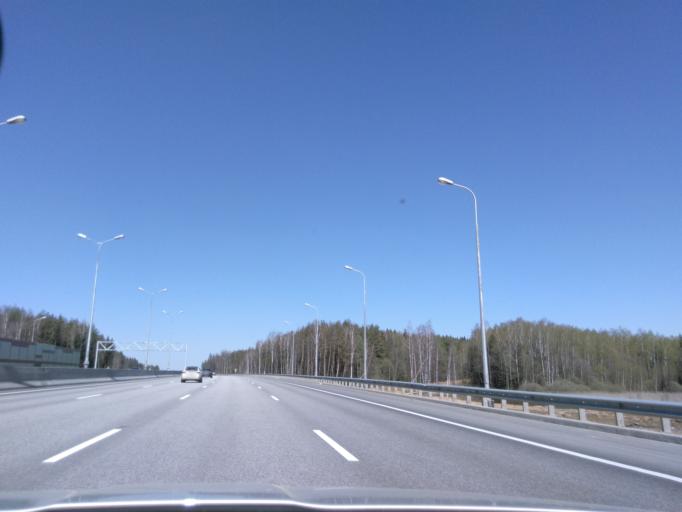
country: RU
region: Moskovskaya
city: Novopodrezkovo
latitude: 55.9652
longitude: 37.3488
